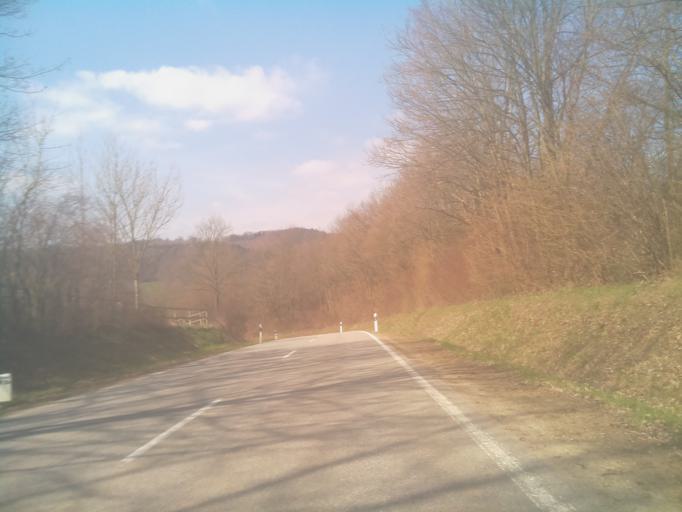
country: DE
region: Hesse
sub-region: Regierungsbezirk Darmstadt
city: Morlenbach
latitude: 49.6063
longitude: 8.7119
